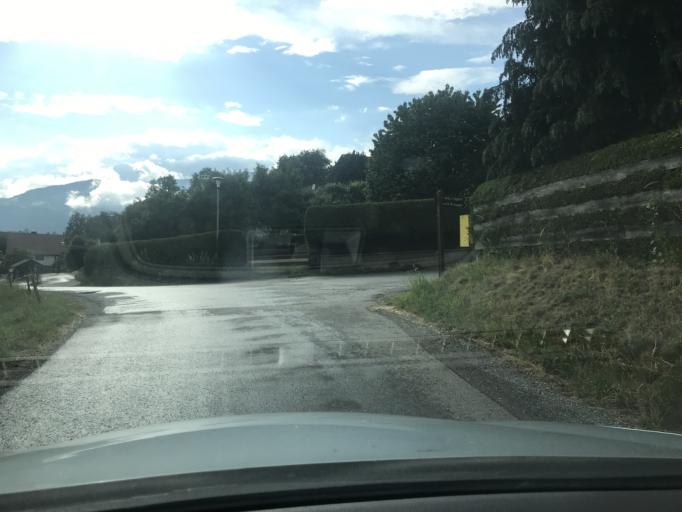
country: AT
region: Styria
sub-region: Politischer Bezirk Murau
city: Sankt Peter am Kammersberg
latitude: 47.1899
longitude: 14.1748
